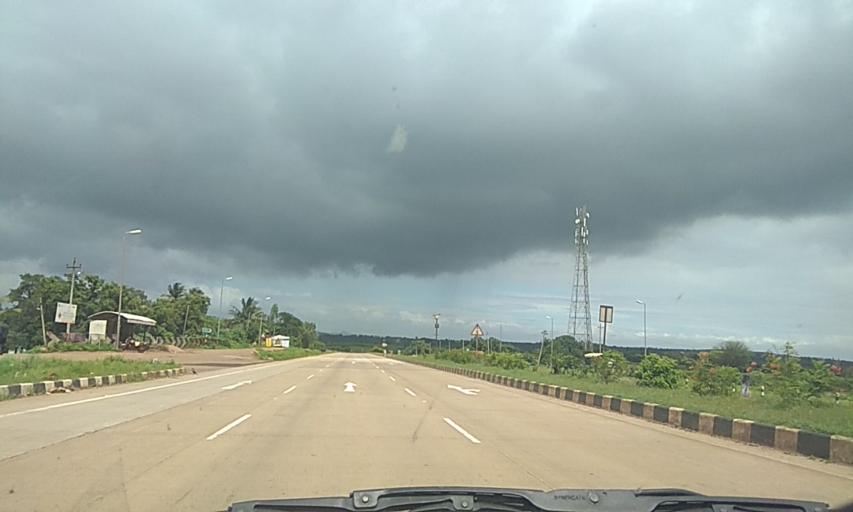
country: IN
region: Karnataka
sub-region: Dharwad
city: Alnavar
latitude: 15.5469
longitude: 74.8645
